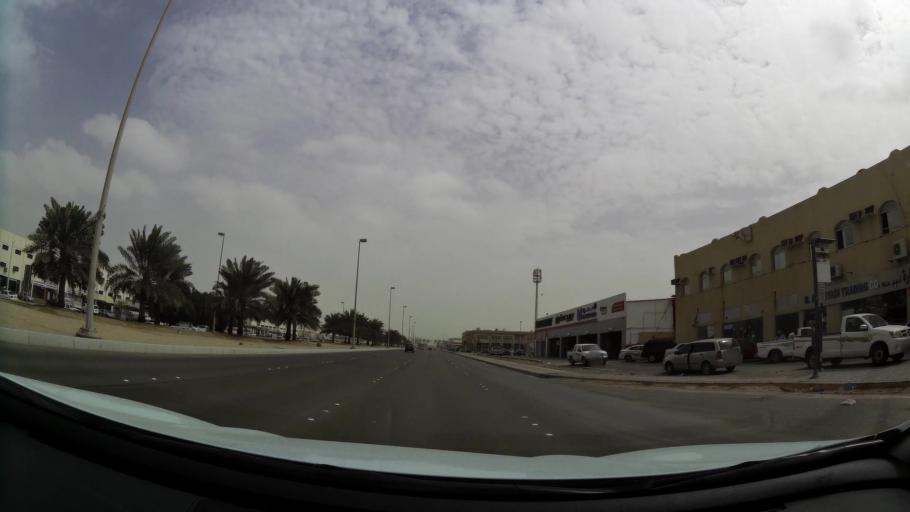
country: AE
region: Abu Dhabi
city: Abu Dhabi
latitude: 24.3725
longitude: 54.4952
